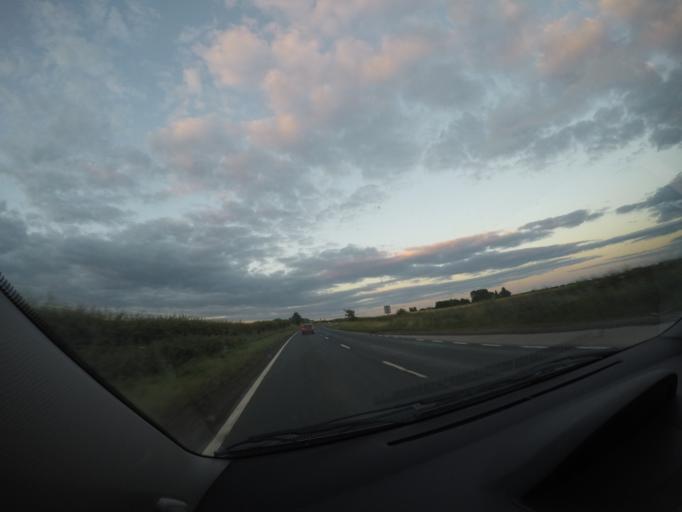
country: GB
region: England
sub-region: City and Borough of Leeds
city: Wetherby
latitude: 54.0098
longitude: -1.3666
